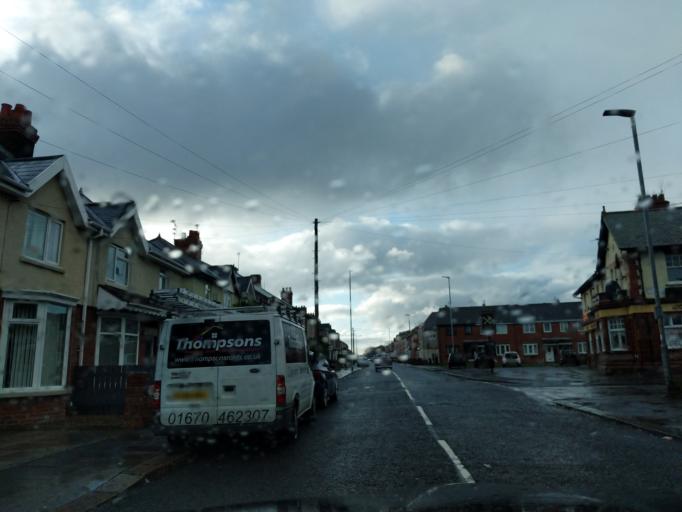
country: GB
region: England
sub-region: Northumberland
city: Blyth
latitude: 55.1223
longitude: -1.5072
